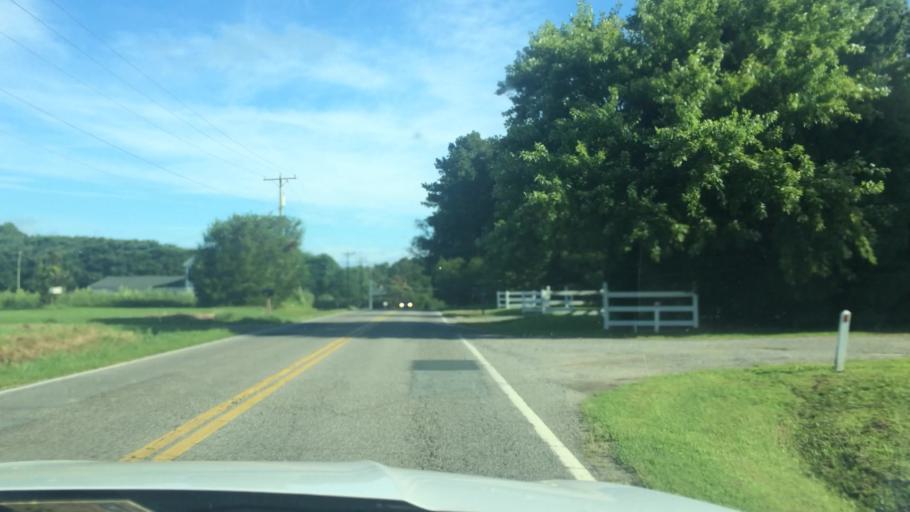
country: US
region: Virginia
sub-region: Middlesex County
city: Deltaville
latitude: 37.5768
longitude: -76.4559
